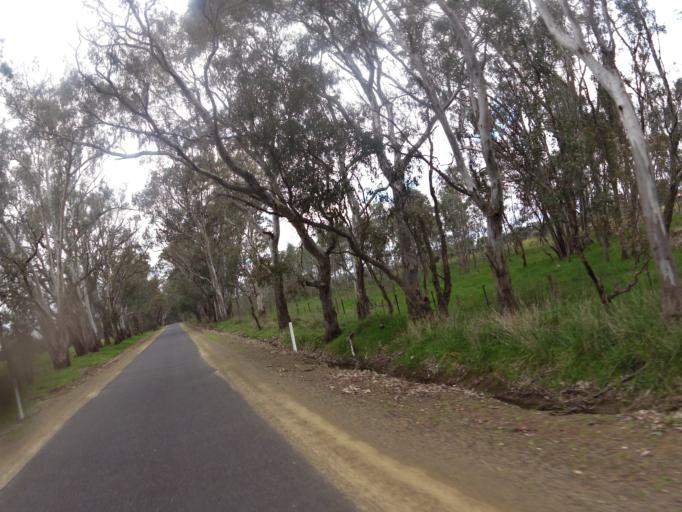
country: AU
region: Victoria
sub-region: Benalla
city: Benalla
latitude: -36.6785
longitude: 145.9602
